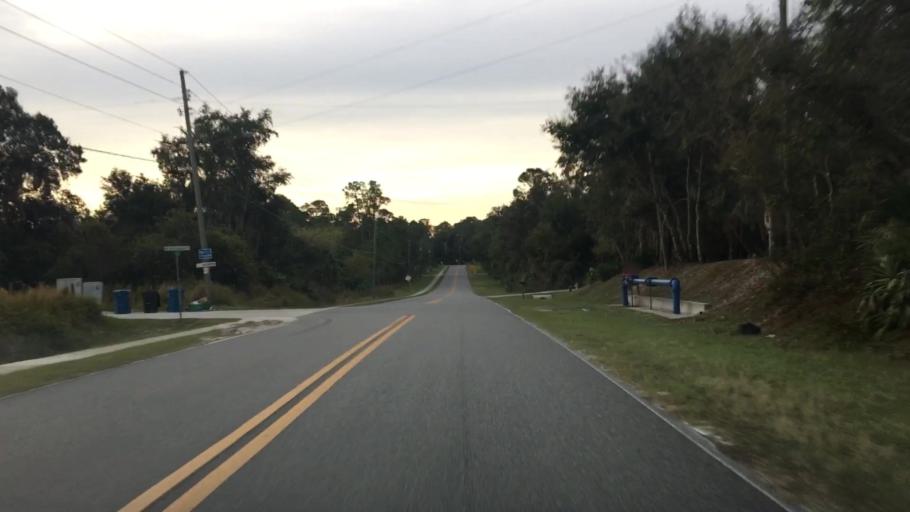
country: US
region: Florida
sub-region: Volusia County
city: Deltona
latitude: 28.8639
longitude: -81.2318
